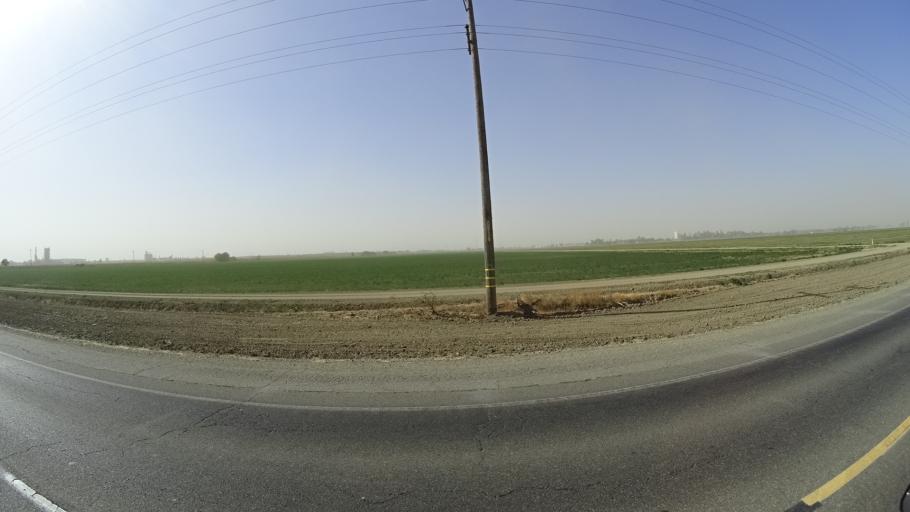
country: US
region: California
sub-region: Yolo County
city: Woodland
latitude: 38.7001
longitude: -121.7280
